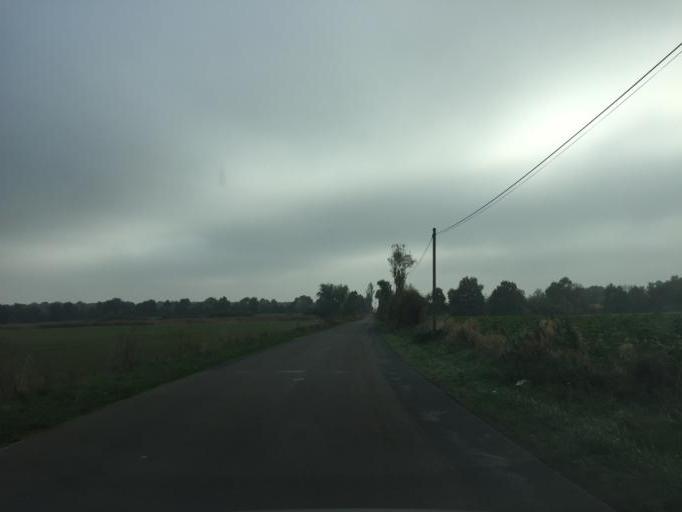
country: FR
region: Rhone-Alpes
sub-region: Departement de l'Ain
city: Saint-Andre-de-Corcy
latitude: 45.9192
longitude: 4.9545
